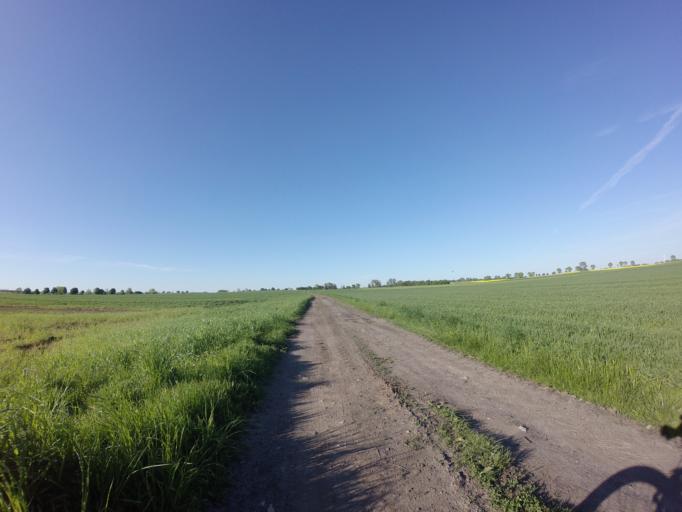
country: PL
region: West Pomeranian Voivodeship
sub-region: Powiat choszczenski
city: Choszczno
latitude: 53.1181
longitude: 15.3658
